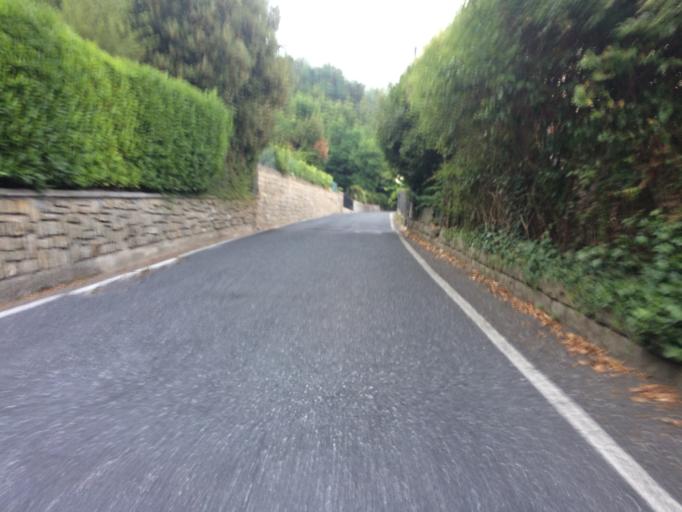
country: IT
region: Liguria
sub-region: Provincia di Imperia
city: Seborga
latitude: 43.8516
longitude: 7.7204
